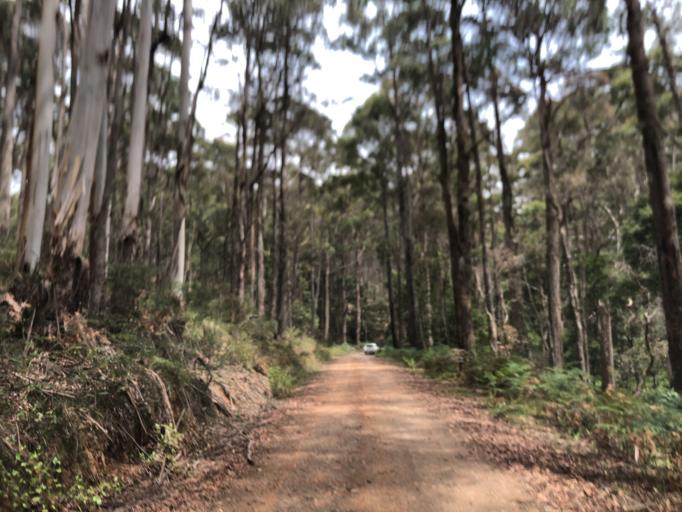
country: AU
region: Victoria
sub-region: Moorabool
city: Bacchus Marsh
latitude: -37.4529
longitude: 144.2510
